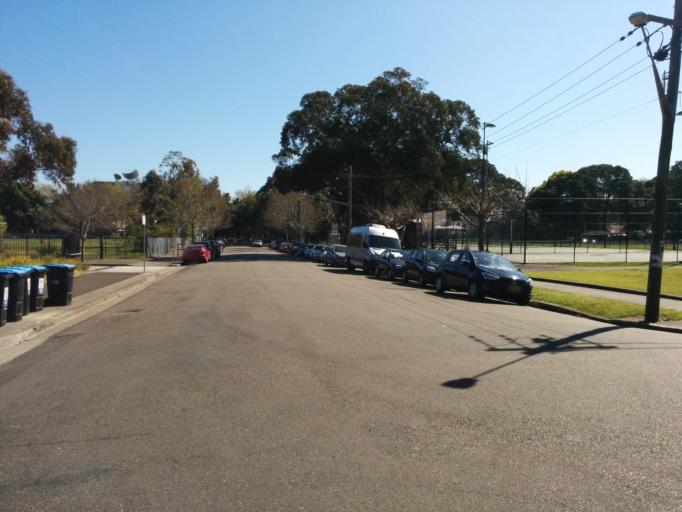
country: AU
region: New South Wales
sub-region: City of Sydney
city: Alexandria
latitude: -33.9012
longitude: 151.1966
